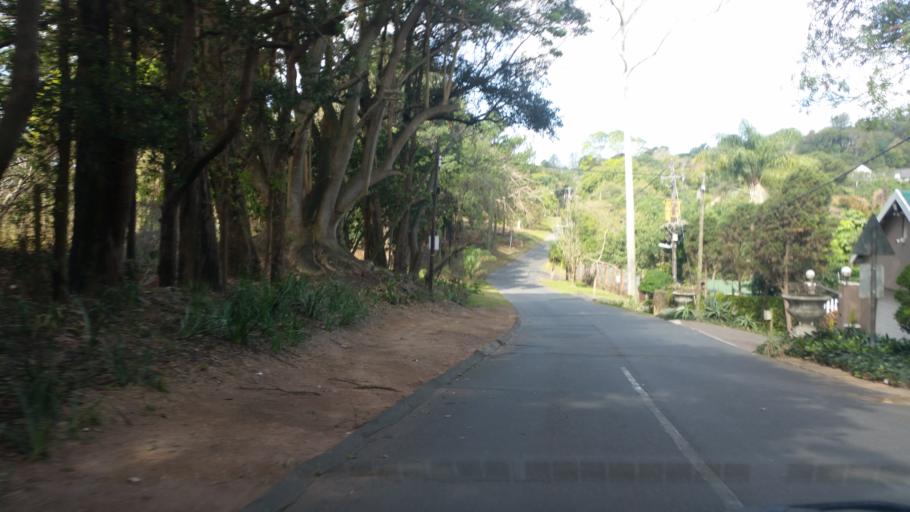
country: ZA
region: KwaZulu-Natal
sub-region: eThekwini Metropolitan Municipality
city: Berea
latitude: -29.8360
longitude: 30.8977
